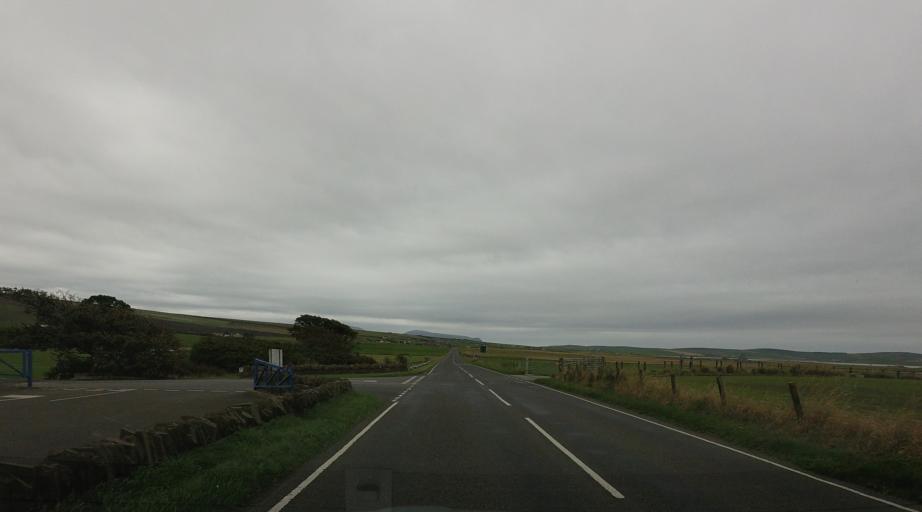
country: GB
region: Scotland
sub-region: Orkney Islands
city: Stromness
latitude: 58.9945
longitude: -3.1869
